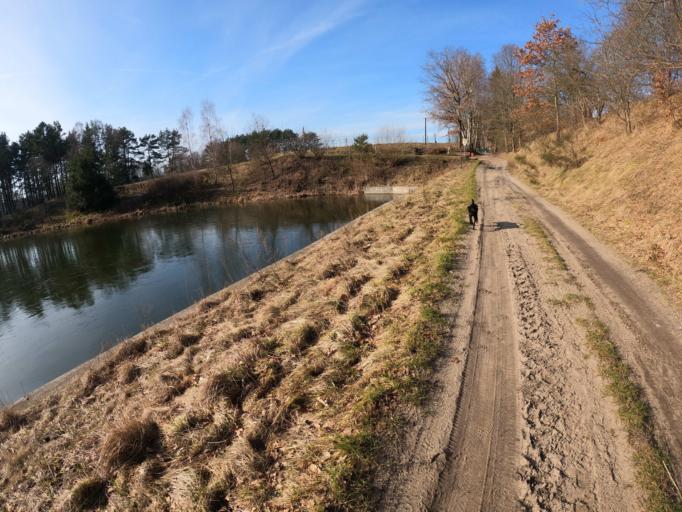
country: PL
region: West Pomeranian Voivodeship
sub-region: Powiat koszalinski
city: Polanow
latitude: 54.1131
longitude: 16.6933
